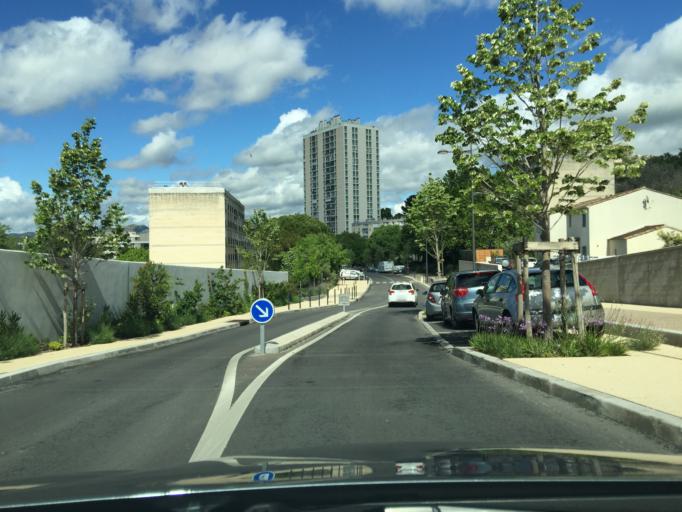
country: FR
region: Provence-Alpes-Cote d'Azur
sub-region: Departement des Bouches-du-Rhone
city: Marseille 11
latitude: 43.2786
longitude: 5.4396
